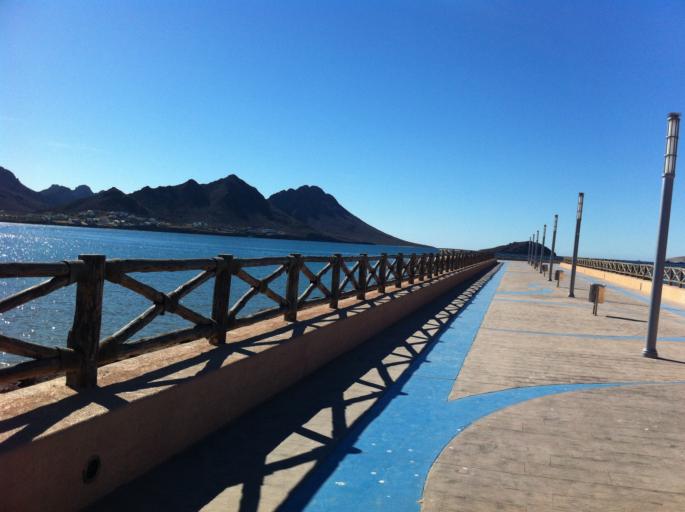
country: MX
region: Sonora
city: Heroica Guaymas
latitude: 27.9267
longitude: -110.9514
